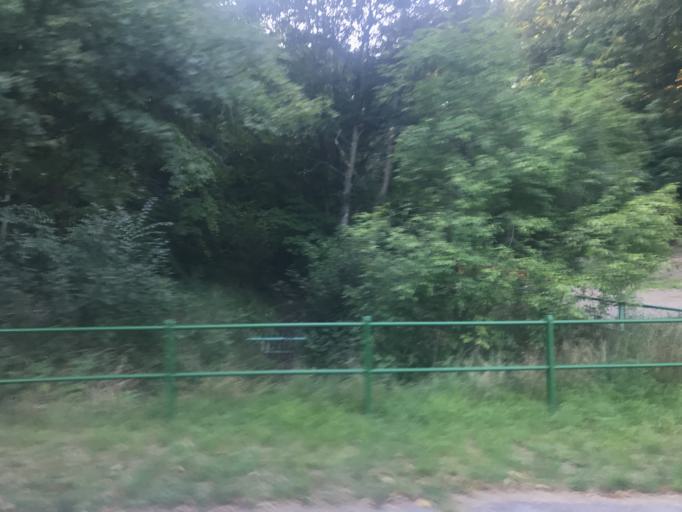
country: AT
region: Lower Austria
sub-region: Politischer Bezirk Wien-Umgebung
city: Klosterneuburg
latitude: 48.2682
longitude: 16.3211
